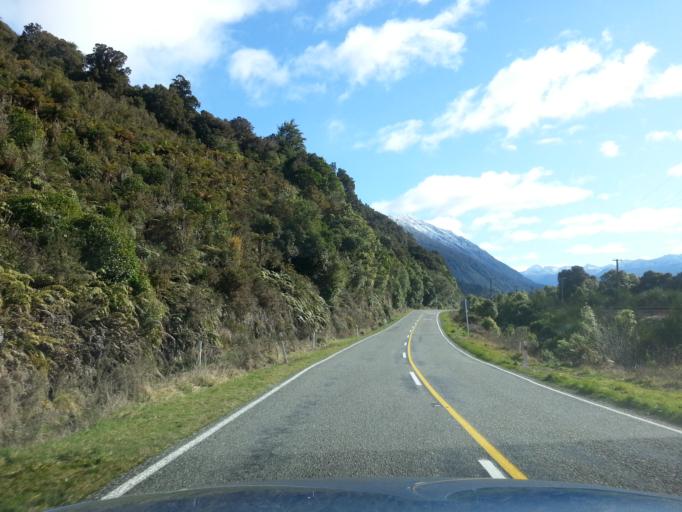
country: NZ
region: West Coast
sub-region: Grey District
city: Greymouth
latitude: -42.7638
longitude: 171.6023
